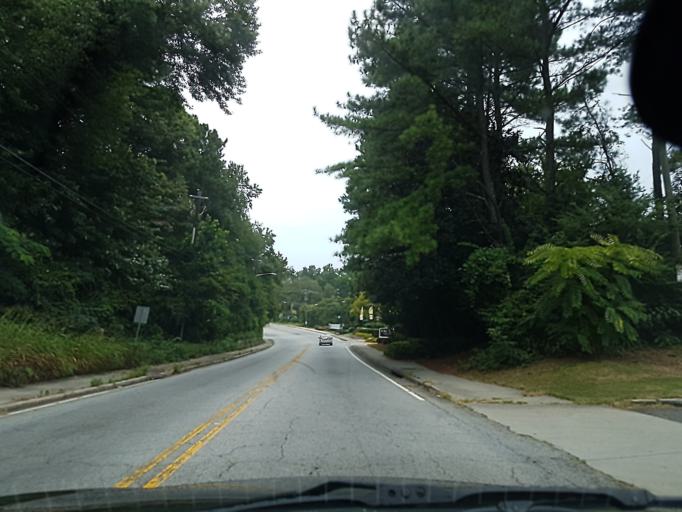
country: US
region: Georgia
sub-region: DeKalb County
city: Scottdale
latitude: 33.8065
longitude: -84.2680
